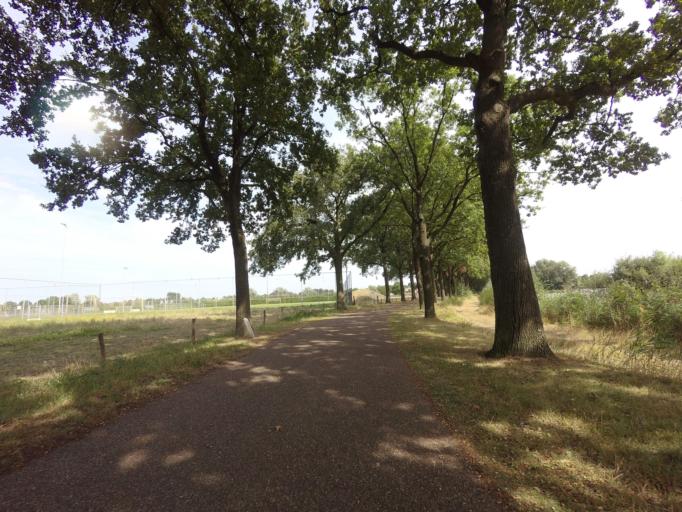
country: NL
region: North Brabant
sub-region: Gemeente Helmond
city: Helmond
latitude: 51.4533
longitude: 5.6960
